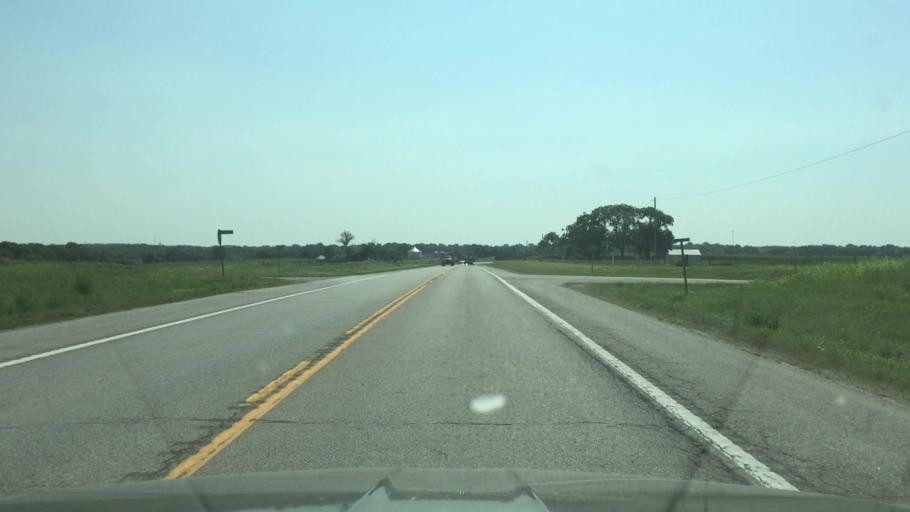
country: US
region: Missouri
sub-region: Pettis County
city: Sedalia
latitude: 38.6916
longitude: -93.0608
